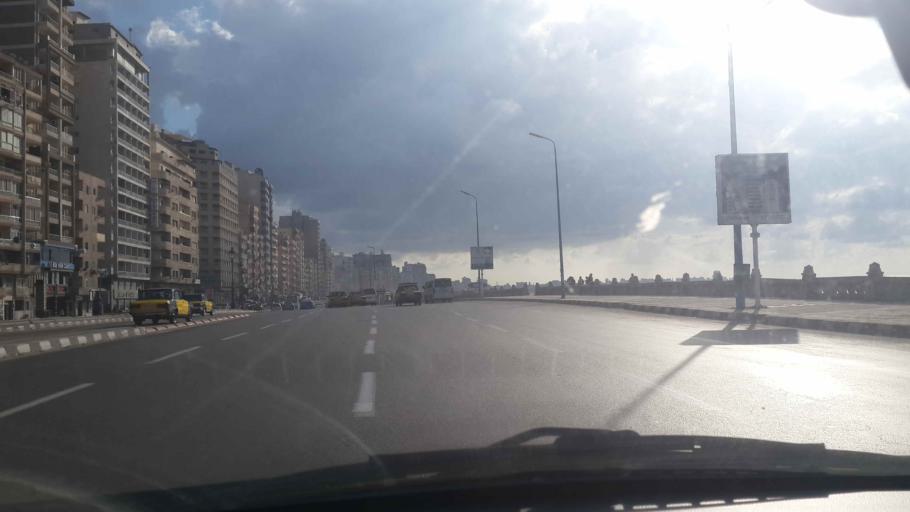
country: EG
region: Alexandria
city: Alexandria
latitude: 31.2260
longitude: 29.9364
